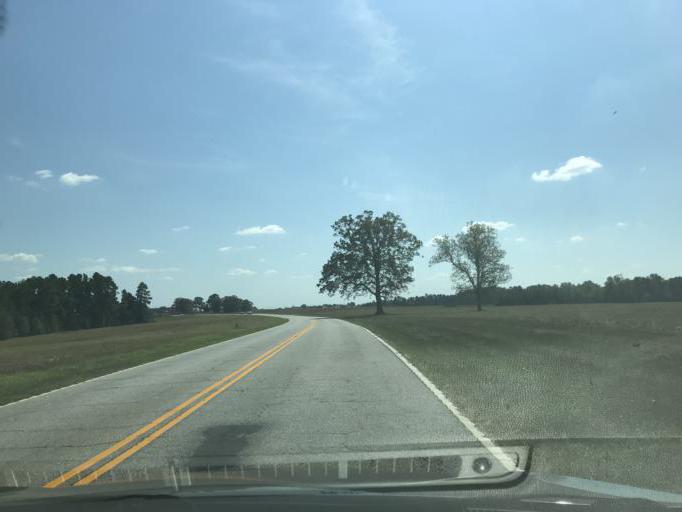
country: US
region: South Carolina
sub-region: Cherokee County
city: Gaffney
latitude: 35.0927
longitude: -81.7110
